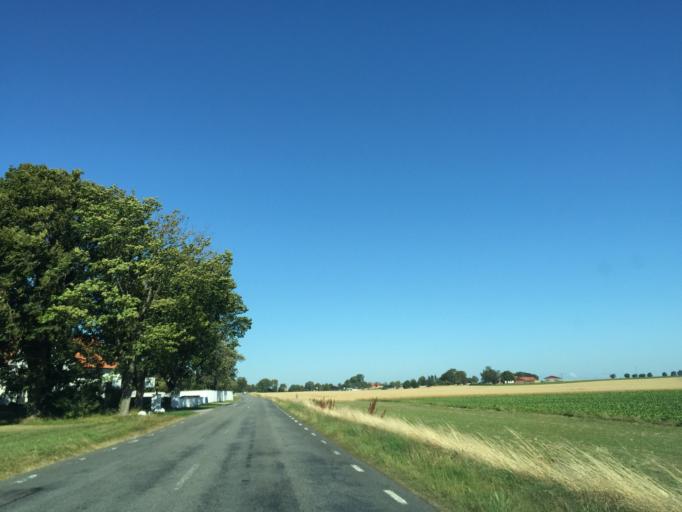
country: SE
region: Skane
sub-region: Ystads Kommun
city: Kopingebro
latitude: 55.4529
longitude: 14.1154
